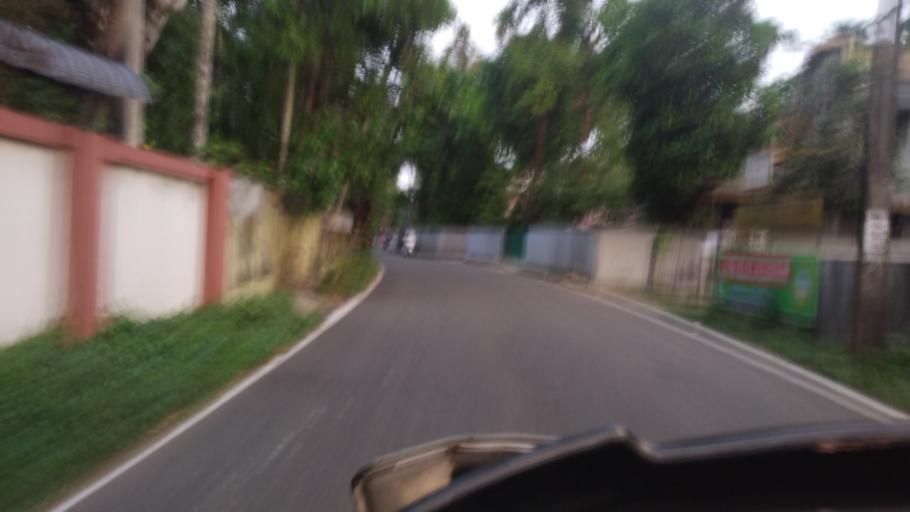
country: IN
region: Kerala
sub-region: Thrissur District
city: Kodungallur
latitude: 10.1604
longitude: 76.2106
